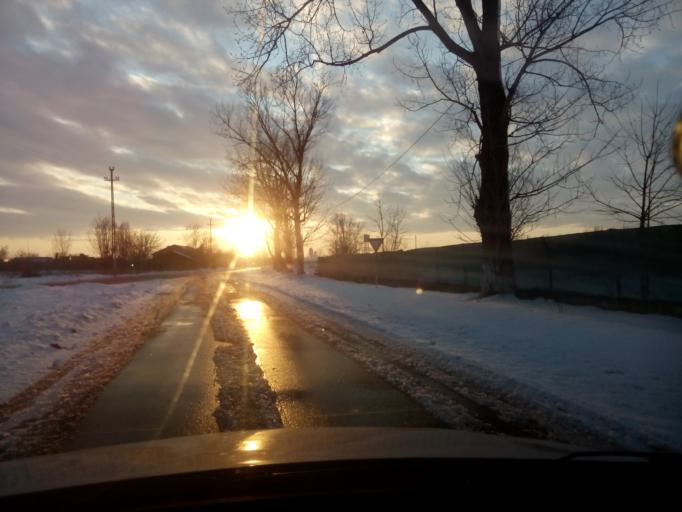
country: RO
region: Calarasi
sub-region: Comuna Luica
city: Luica
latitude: 44.2331
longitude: 26.5941
